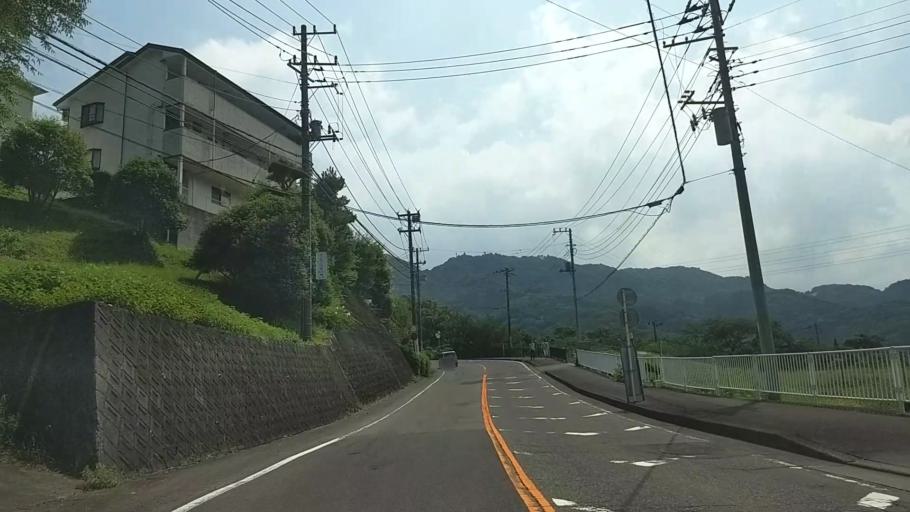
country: JP
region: Shizuoka
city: Ito
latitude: 34.9379
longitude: 139.0845
